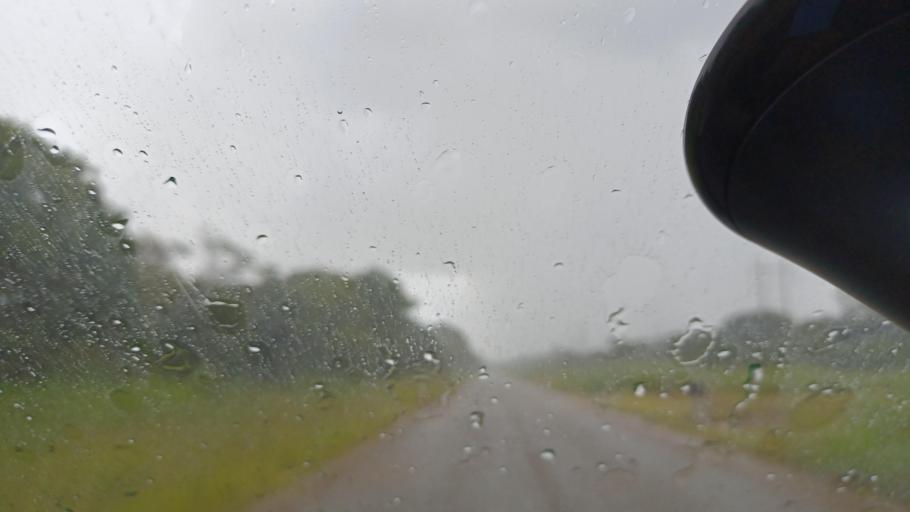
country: ZM
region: North-Western
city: Kasempa
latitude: -13.0906
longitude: 25.9453
